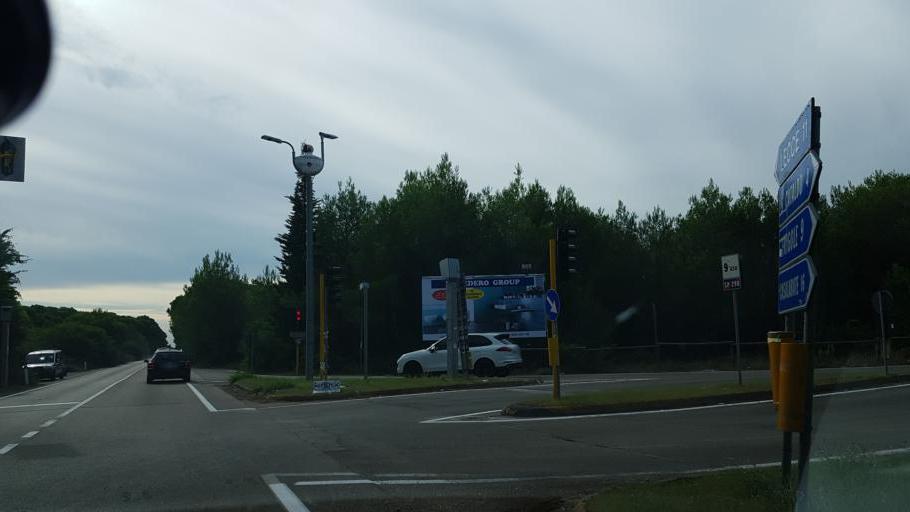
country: IT
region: Apulia
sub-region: Provincia di Lecce
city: Struda
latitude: 40.3683
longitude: 18.3100
